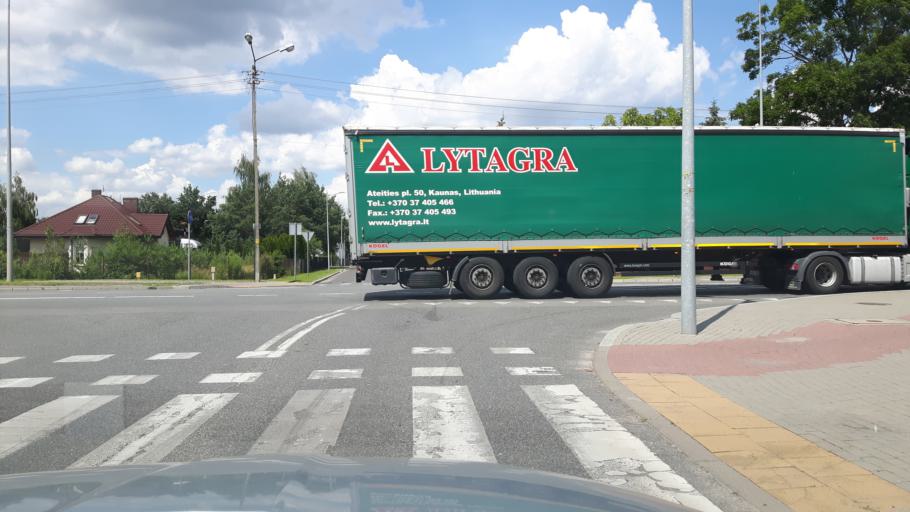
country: PL
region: Masovian Voivodeship
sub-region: Powiat wyszkowski
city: Wyszkow
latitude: 52.5893
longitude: 21.4354
